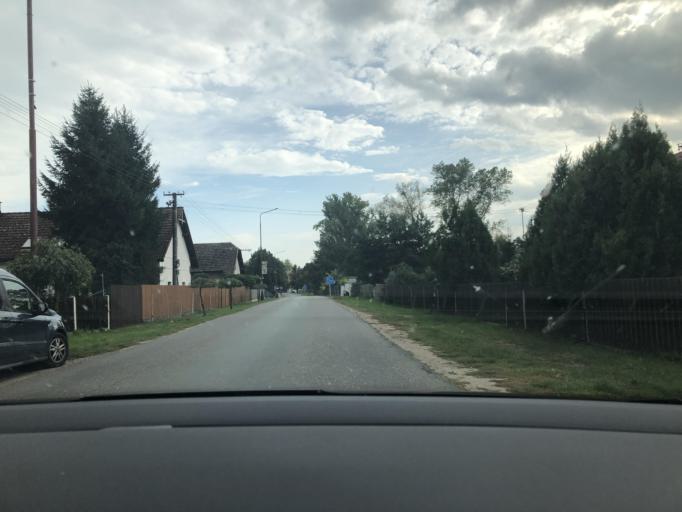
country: CZ
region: Pardubicky
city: Recany nad Labem
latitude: 50.0615
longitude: 15.4834
